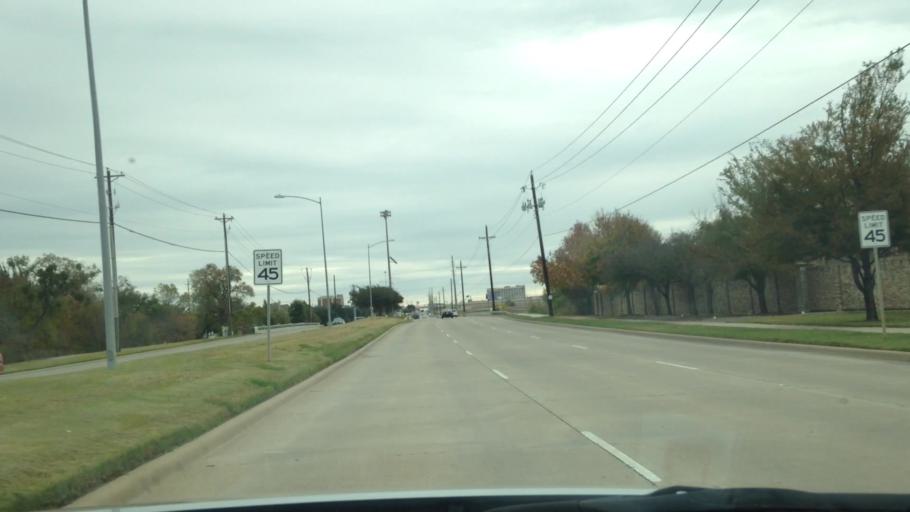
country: US
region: Texas
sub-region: Collin County
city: Allen
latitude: 33.1298
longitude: -96.6715
